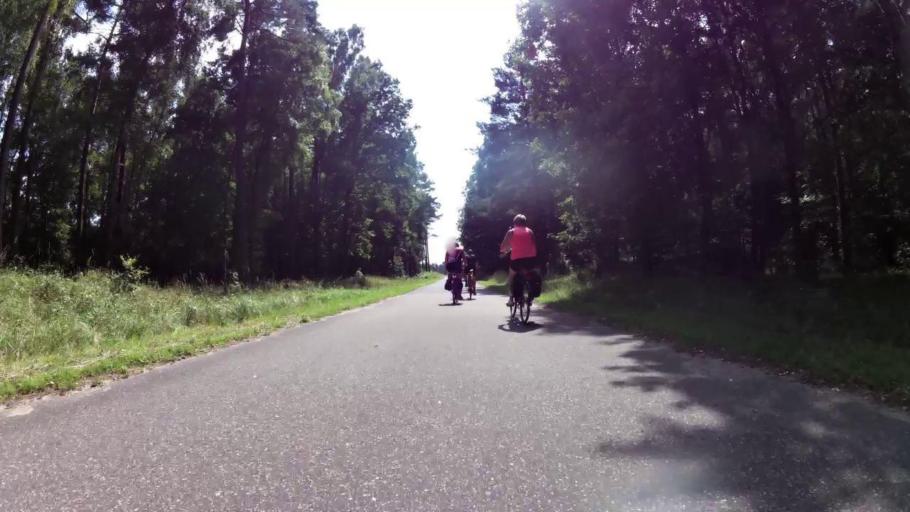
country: PL
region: West Pomeranian Voivodeship
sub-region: Powiat choszczenski
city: Drawno
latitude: 53.3381
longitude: 15.7009
